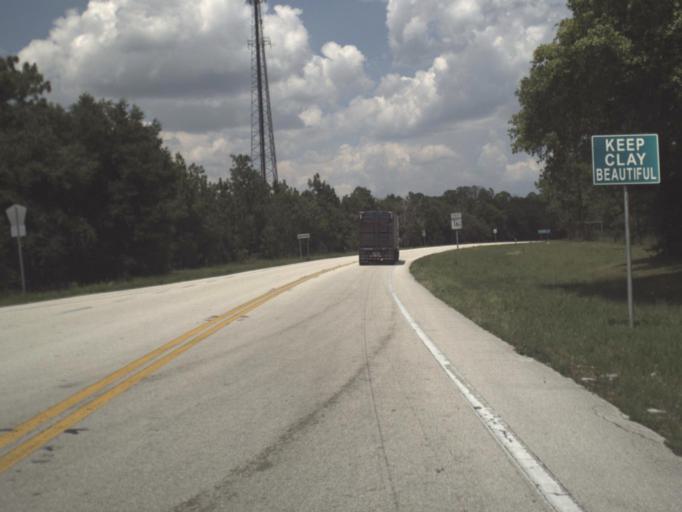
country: US
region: Florida
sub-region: Bradford County
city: Starke
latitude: 29.9811
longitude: -82.0132
